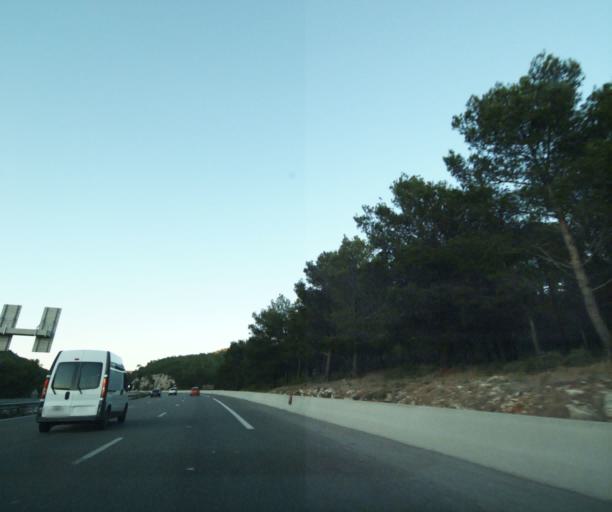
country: FR
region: Provence-Alpes-Cote d'Azur
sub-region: Departement des Bouches-du-Rhone
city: Roquefort-la-Bedoule
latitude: 43.2149
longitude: 5.5823
